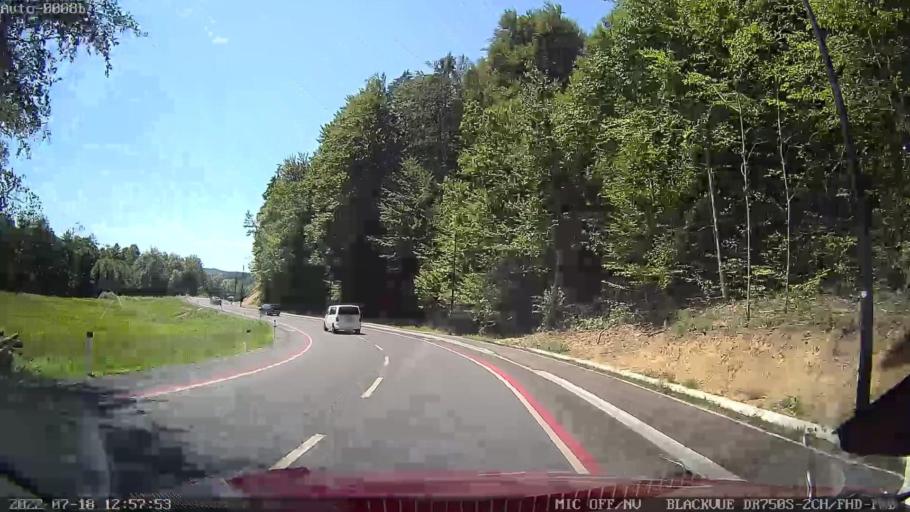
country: SI
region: Dobrova-Horjul-Polhov Gradec
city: Dobrova
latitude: 46.0659
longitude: 14.4207
